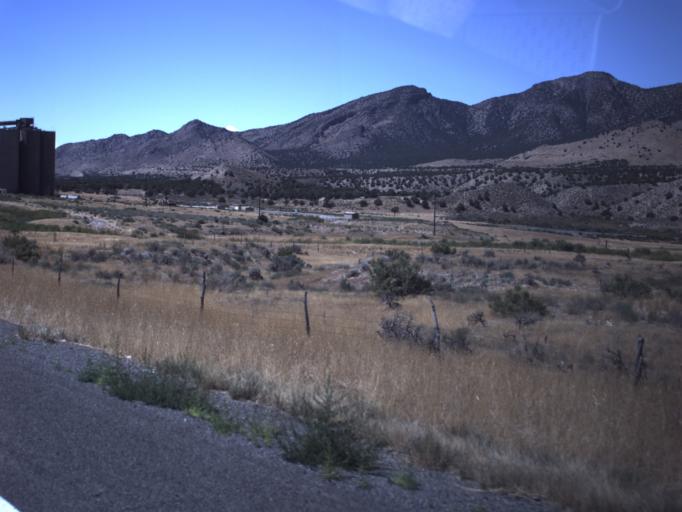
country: US
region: Utah
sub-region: Juab County
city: Nephi
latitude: 39.5683
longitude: -112.1926
